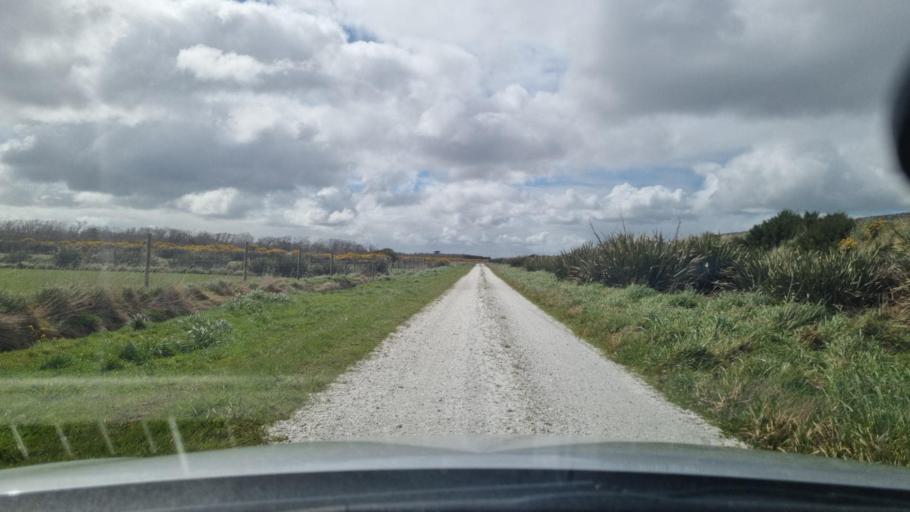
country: NZ
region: Southland
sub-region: Invercargill City
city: Bluff
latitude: -46.5330
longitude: 168.3047
